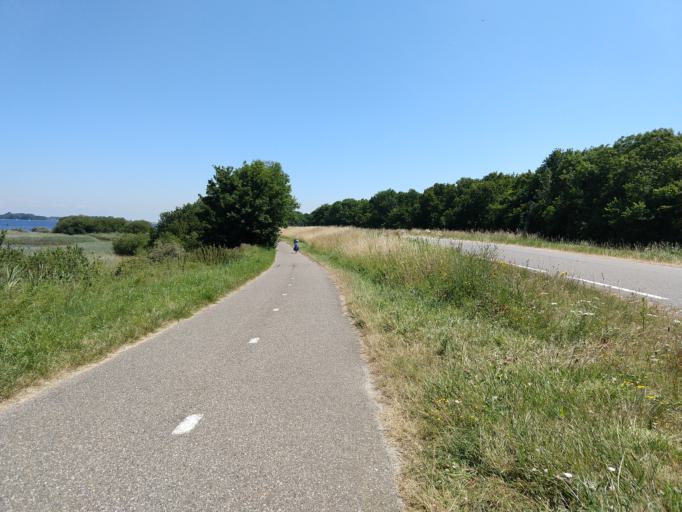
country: NL
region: Zeeland
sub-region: Gemeente Veere
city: Veere
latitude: 51.5628
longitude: 3.6379
